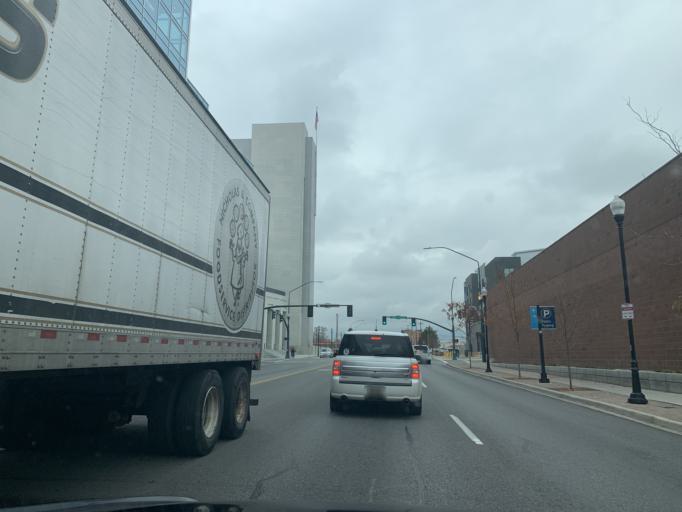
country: US
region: Utah
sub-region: Utah County
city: Provo
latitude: 40.2345
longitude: -111.6622
